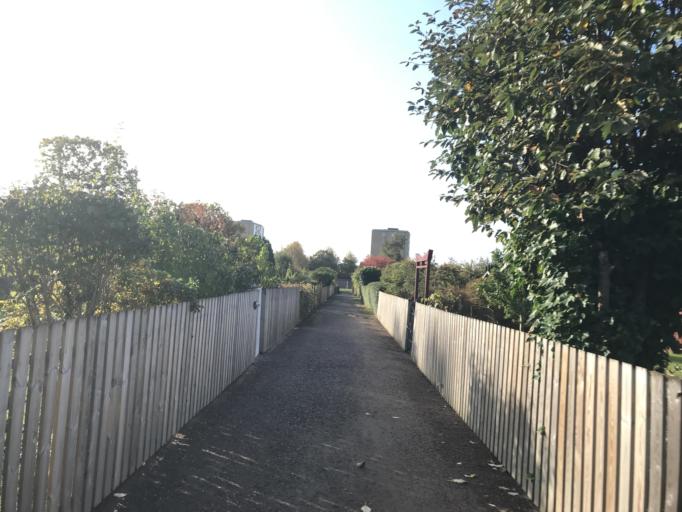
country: SE
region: Skane
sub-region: Landskrona
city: Landskrona
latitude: 55.8849
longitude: 12.8265
